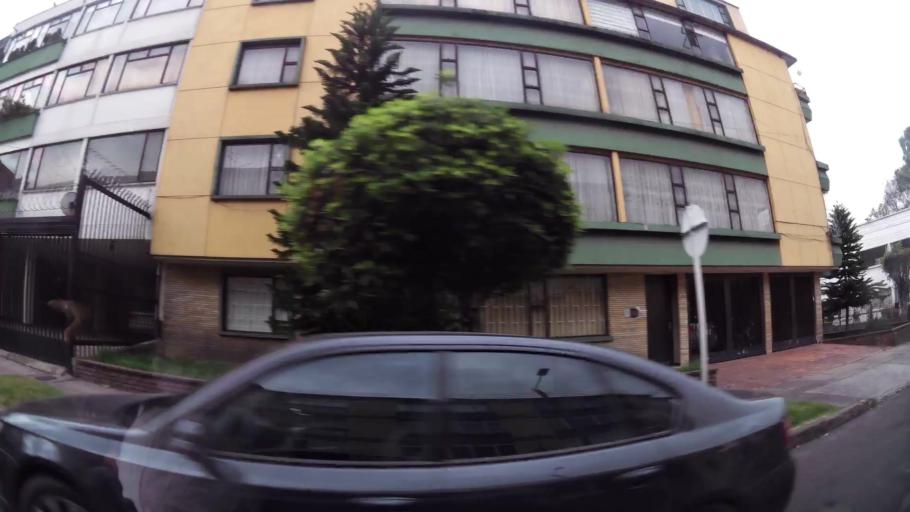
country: CO
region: Bogota D.C.
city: Barrio San Luis
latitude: 4.6527
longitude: -74.0601
